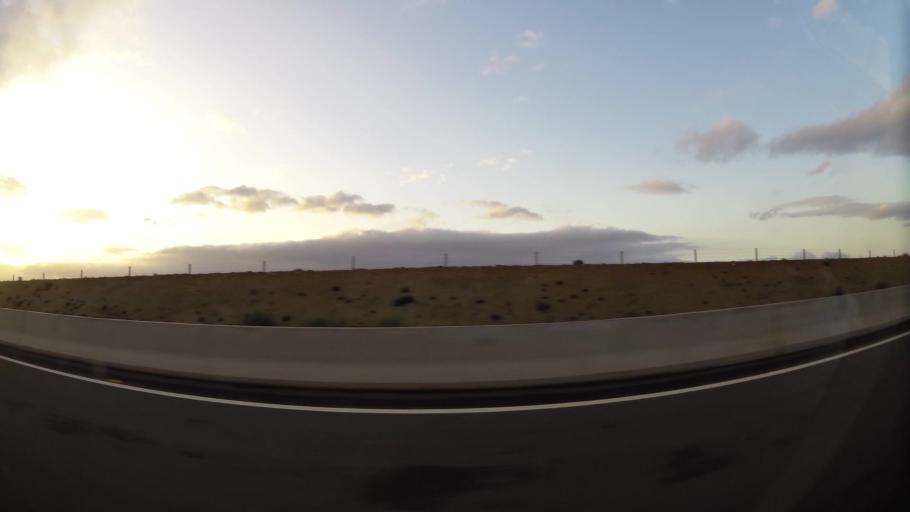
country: MA
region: Oriental
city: Taourirt
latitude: 34.5493
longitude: -2.8792
